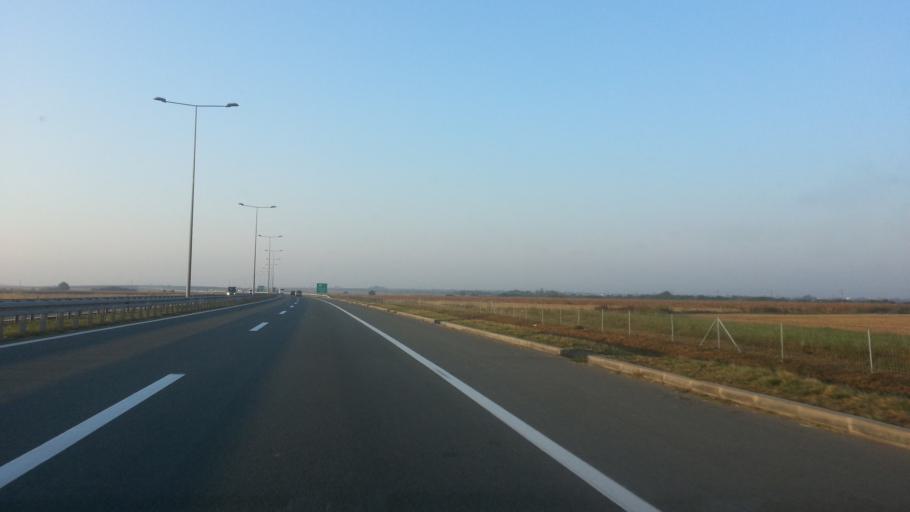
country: RS
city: Dobanovci
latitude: 44.8587
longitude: 20.2501
